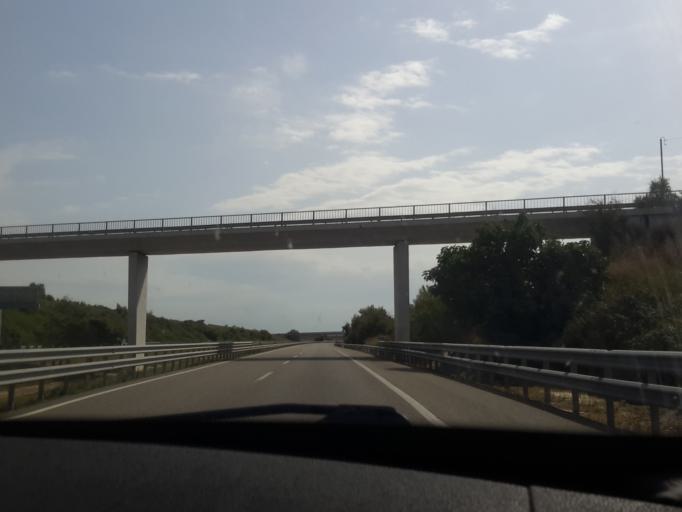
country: ES
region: Catalonia
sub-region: Provincia de Lleida
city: Sunyer
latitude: 41.5488
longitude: 0.5811
